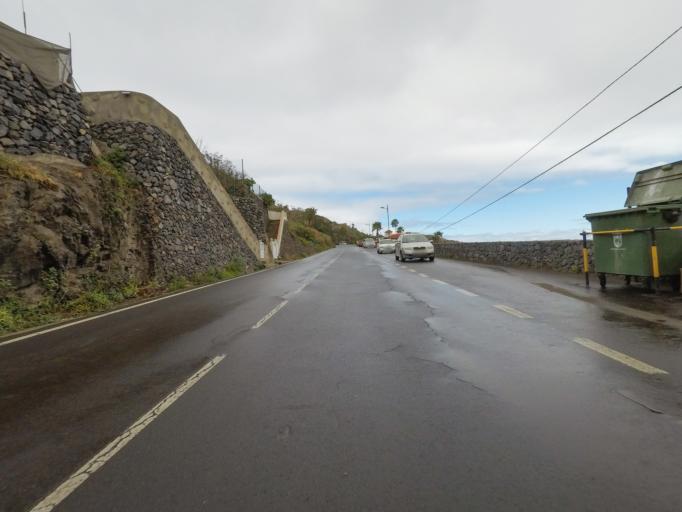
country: ES
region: Canary Islands
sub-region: Provincia de Santa Cruz de Tenerife
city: Agulo
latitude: 28.1856
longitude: -17.2232
